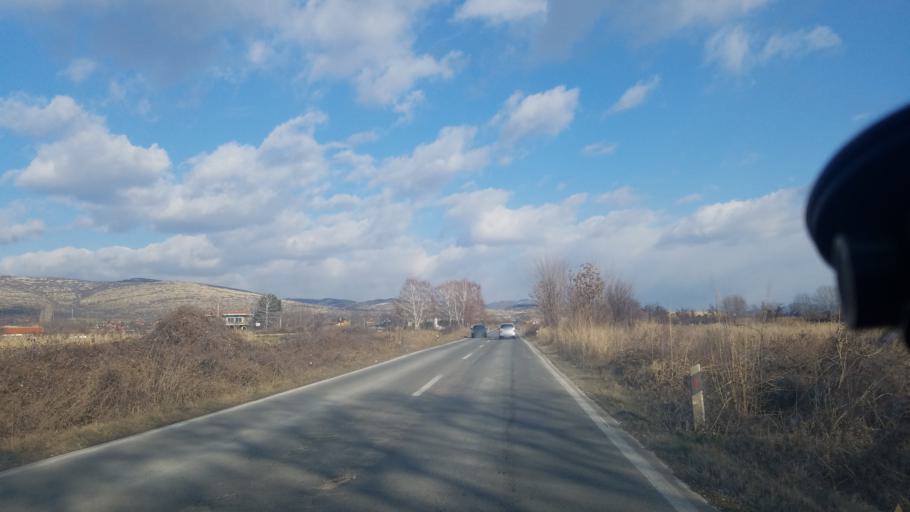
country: MK
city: Obleshevo
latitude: 41.8969
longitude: 22.3593
